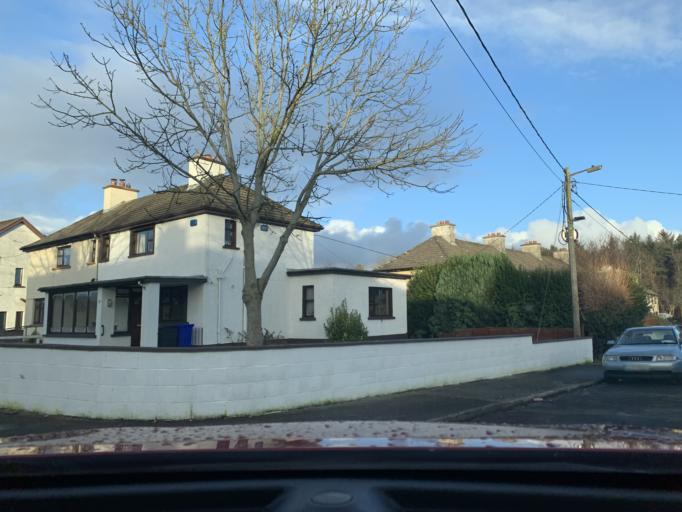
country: IE
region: Connaught
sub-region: Sligo
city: Sligo
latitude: 54.2681
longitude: -8.4577
